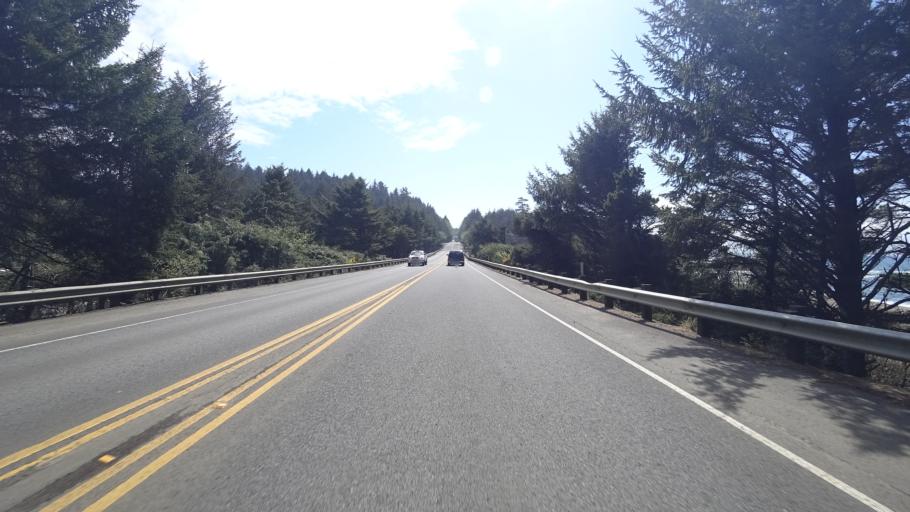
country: US
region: Oregon
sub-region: Lincoln County
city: Lincoln Beach
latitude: 44.8399
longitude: -124.0505
